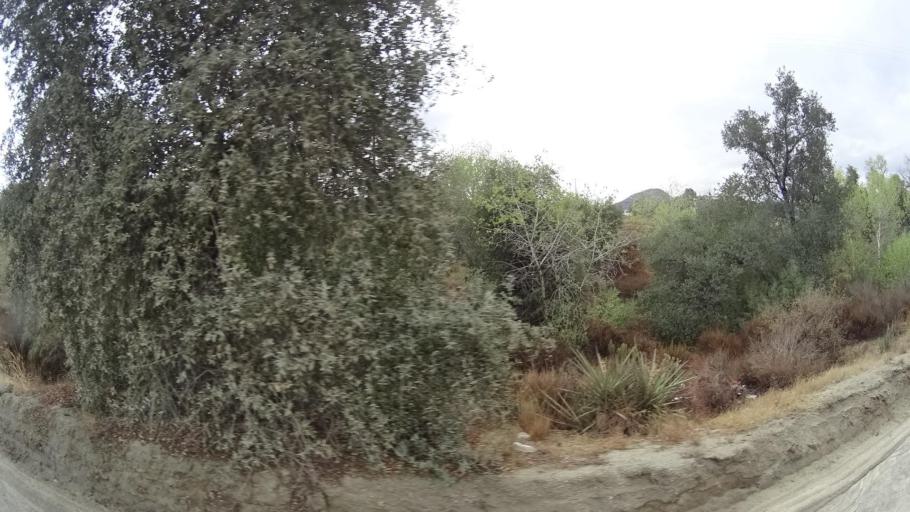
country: MX
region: Baja California
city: Tecate
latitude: 32.5863
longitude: -116.6205
